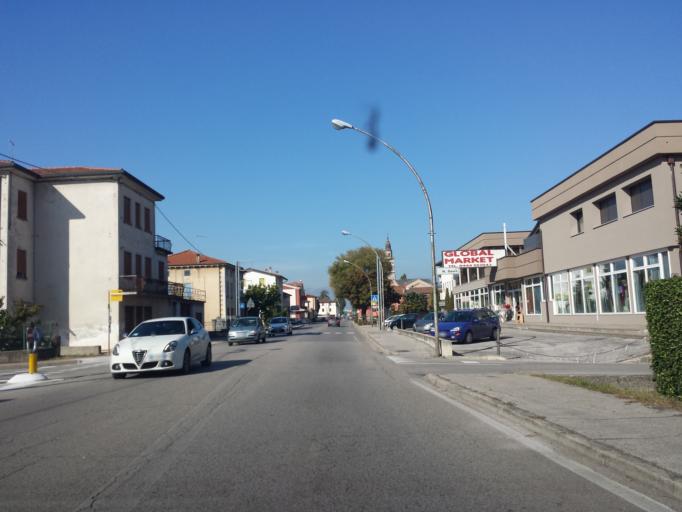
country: IT
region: Veneto
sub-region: Provincia di Vicenza
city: Motta
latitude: 45.5956
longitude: 11.4966
